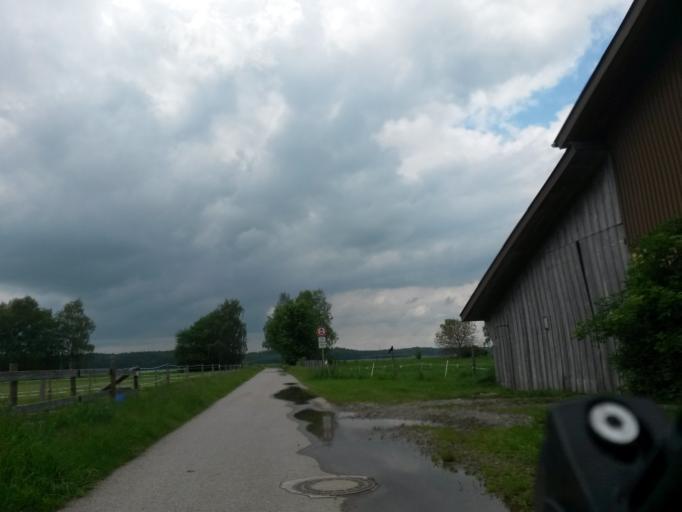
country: DE
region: Baden-Wuerttemberg
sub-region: Tuebingen Region
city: Bad Waldsee
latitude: 47.9353
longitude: 9.8136
